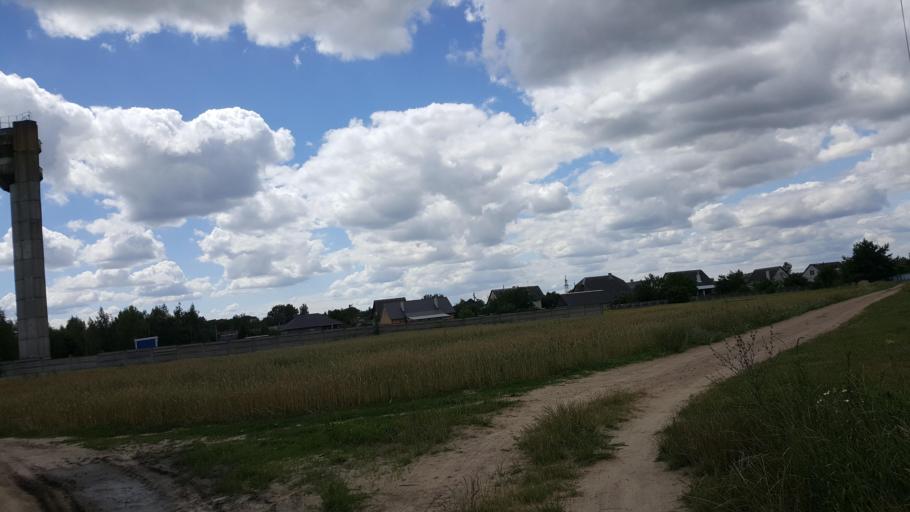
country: BY
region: Brest
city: Kamyanyets
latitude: 52.3217
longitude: 23.9302
